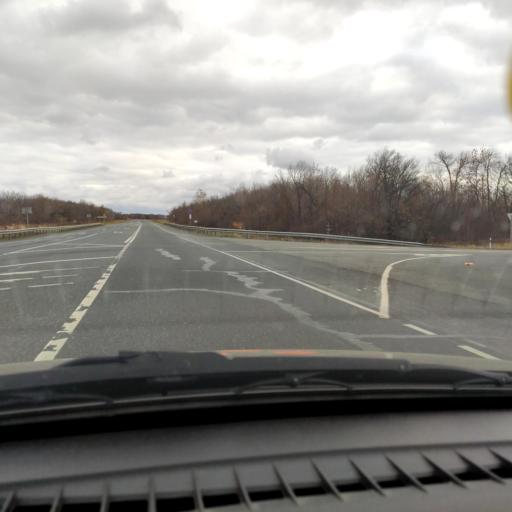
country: RU
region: Samara
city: Mezhdurechensk
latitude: 53.2584
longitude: 49.0744
